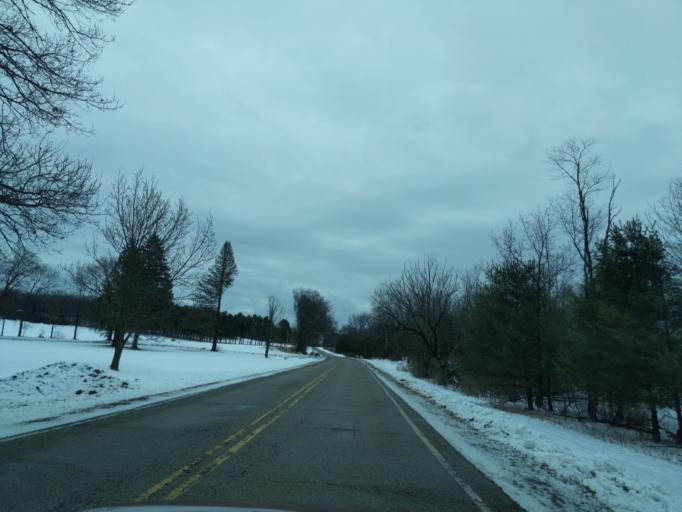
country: US
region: Wisconsin
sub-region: Marquette County
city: Montello
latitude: 43.9130
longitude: -89.3549
